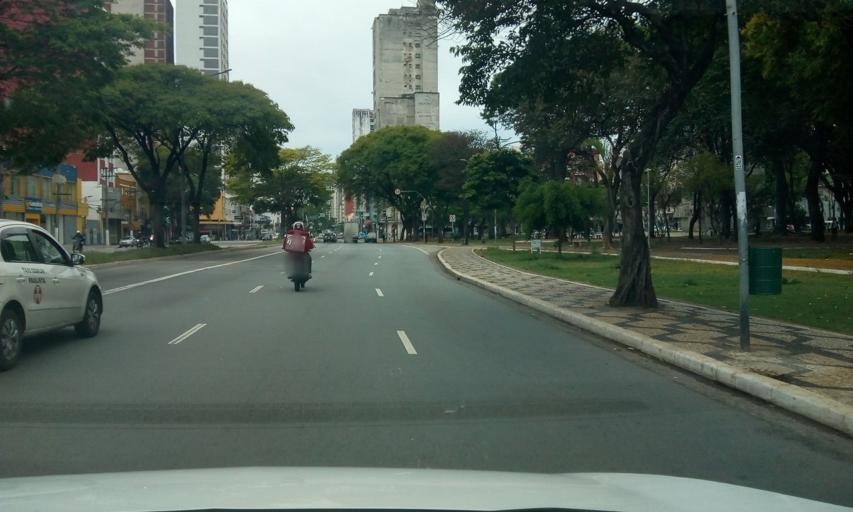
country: BR
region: Sao Paulo
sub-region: Sao Paulo
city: Sao Paulo
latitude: -23.5351
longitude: -46.6436
